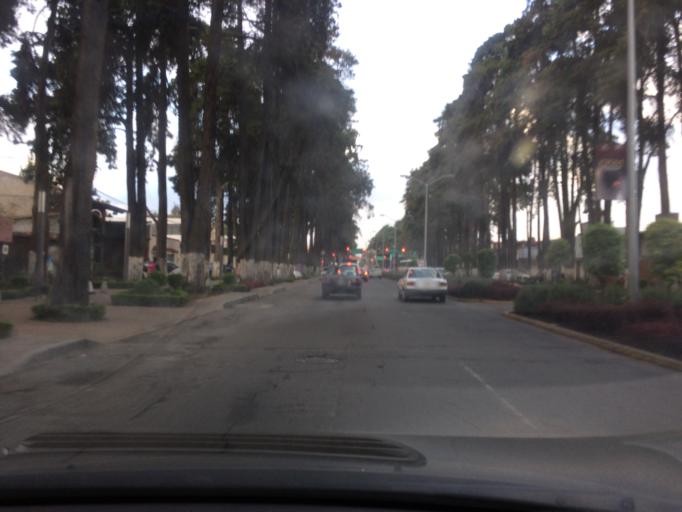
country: MX
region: Mexico
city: Toluca
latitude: 19.2751
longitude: -99.6595
